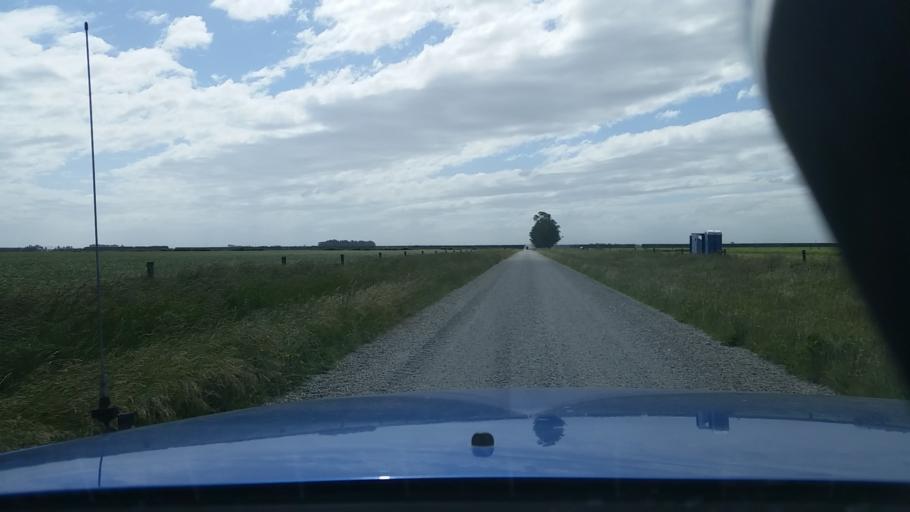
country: NZ
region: Canterbury
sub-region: Ashburton District
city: Ashburton
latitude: -43.9597
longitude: 171.9154
